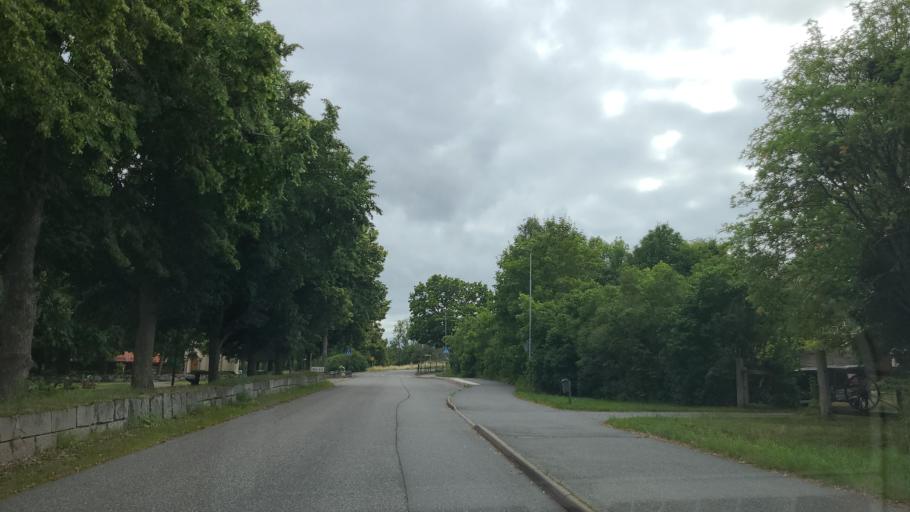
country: SE
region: Stockholm
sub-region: Upplands-Bro Kommun
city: Bro
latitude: 59.5069
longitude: 17.6262
